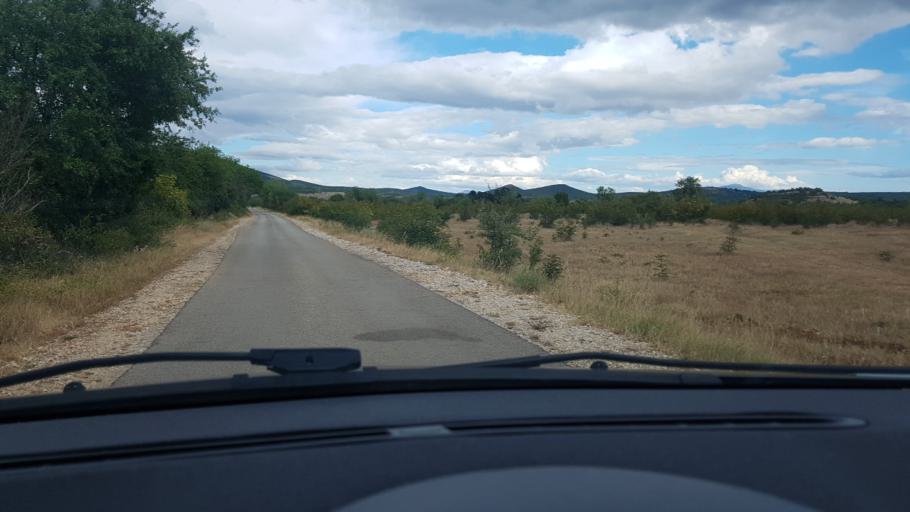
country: HR
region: Sibensko-Kniniska
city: Kistanje
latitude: 44.1080
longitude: 15.9312
